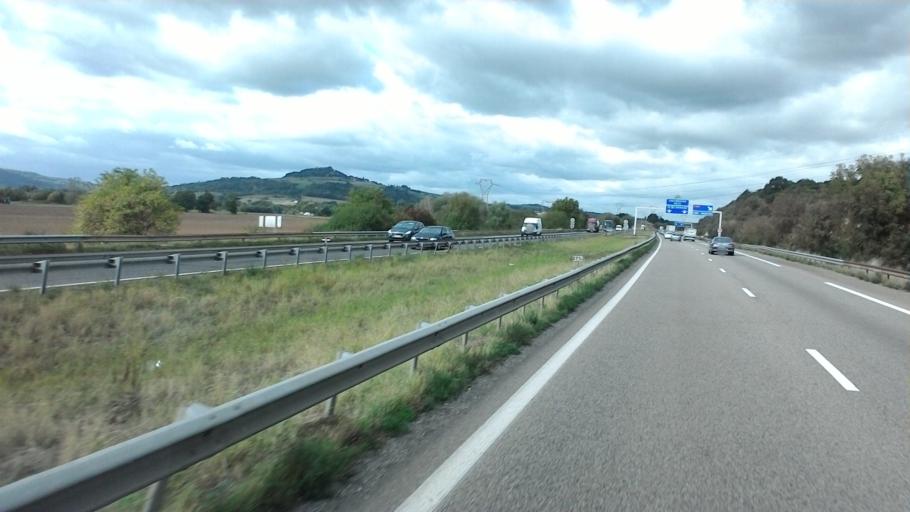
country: FR
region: Lorraine
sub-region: Departement de Meurthe-et-Moselle
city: Dieulouard
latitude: 48.8763
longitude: 6.0964
